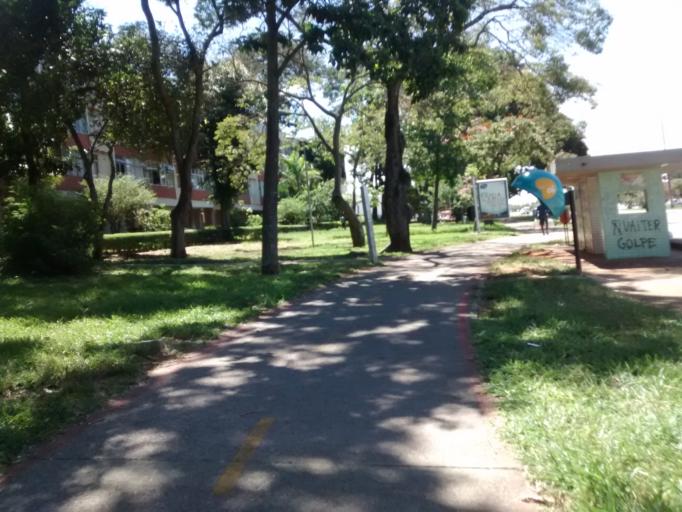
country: BR
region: Federal District
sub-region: Brasilia
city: Brasilia
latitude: -15.8162
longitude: -47.8901
